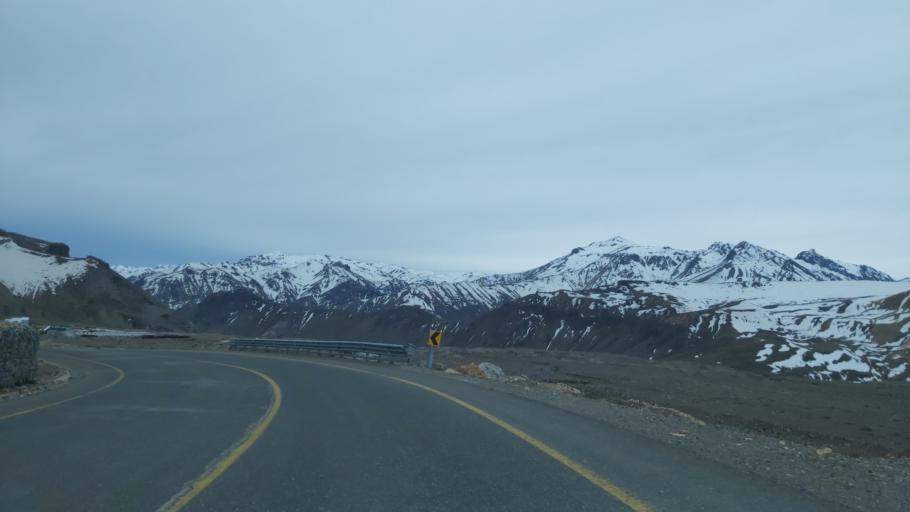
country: CL
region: Maule
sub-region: Provincia de Linares
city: Colbun
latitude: -35.9730
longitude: -70.5640
